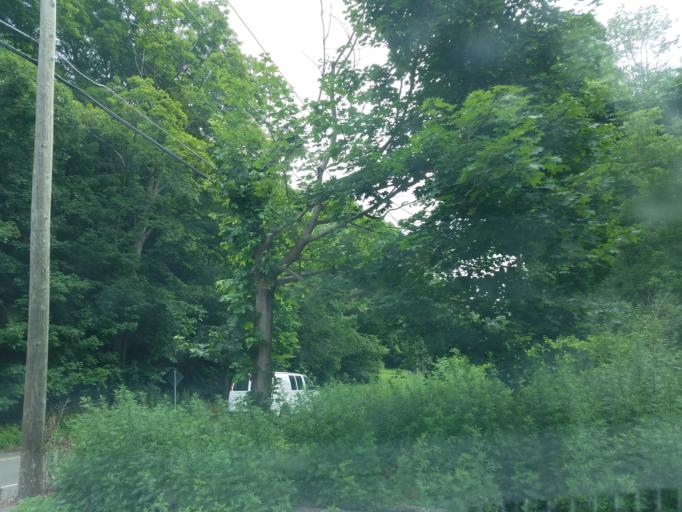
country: US
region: Connecticut
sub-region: Litchfield County
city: Thomaston
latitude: 41.6765
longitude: -73.0703
